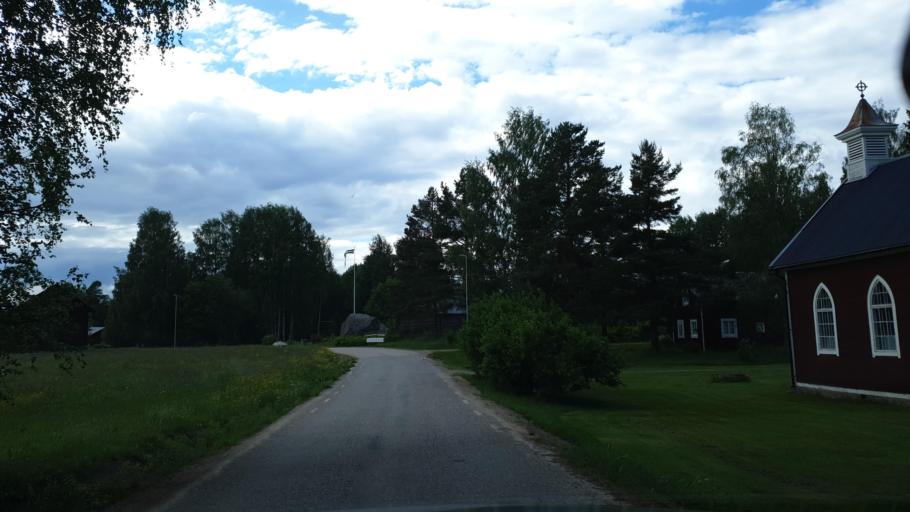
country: SE
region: Jaemtland
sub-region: Harjedalens Kommun
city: Sveg
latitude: 61.7982
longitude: 14.6425
